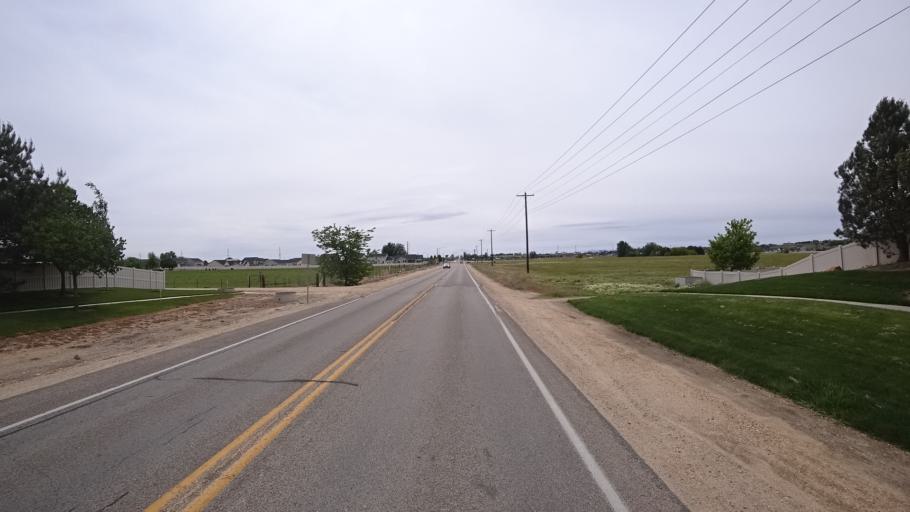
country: US
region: Idaho
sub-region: Ada County
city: Meridian
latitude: 43.5652
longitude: -116.3544
